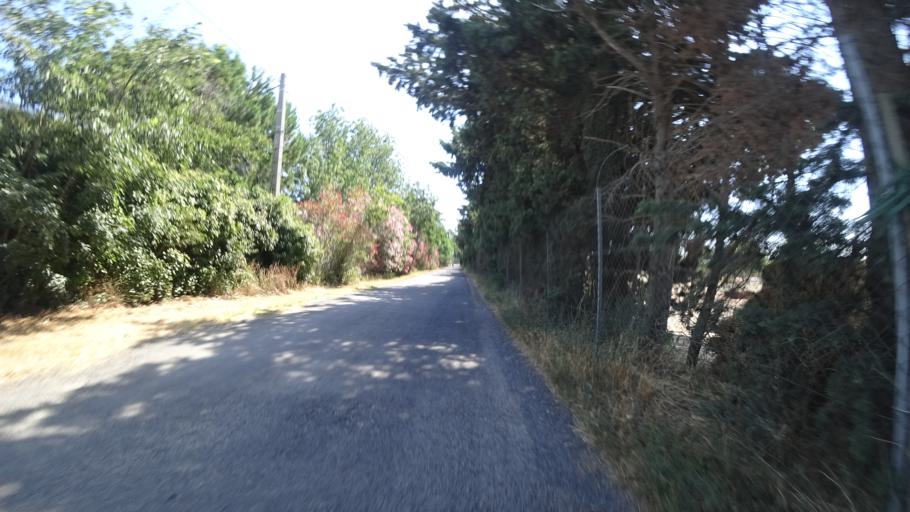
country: FR
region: Languedoc-Roussillon
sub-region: Departement des Pyrenees-Orientales
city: Rivesaltes
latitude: 42.7747
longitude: 2.8808
